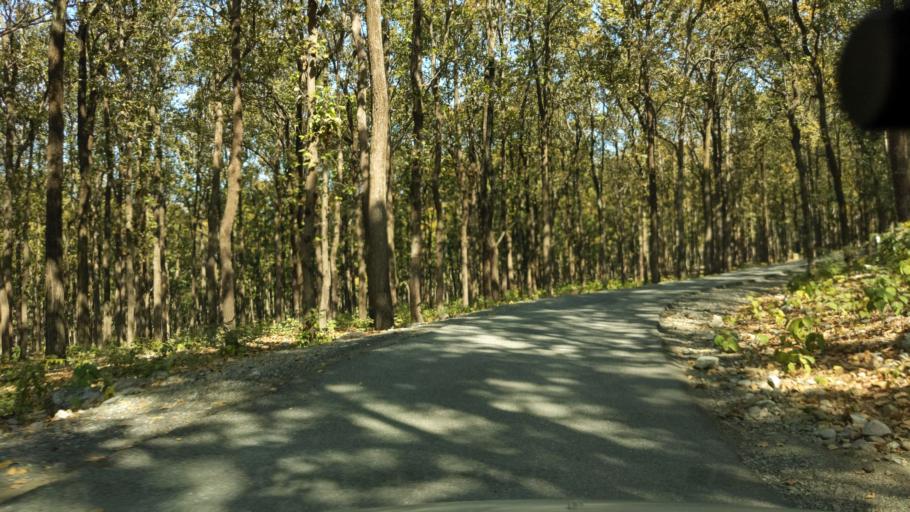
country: IN
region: Uttarakhand
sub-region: Naini Tal
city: Ramnagar
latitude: 29.4672
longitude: 79.2328
